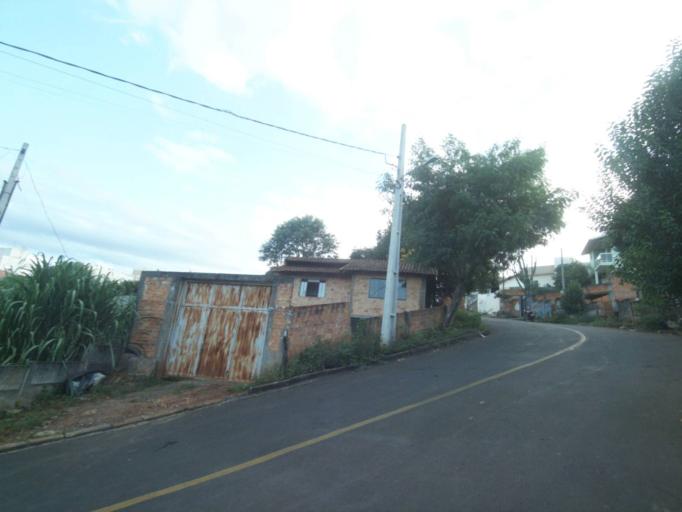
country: BR
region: Parana
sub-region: Telemaco Borba
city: Telemaco Borba
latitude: -24.3256
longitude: -50.6397
